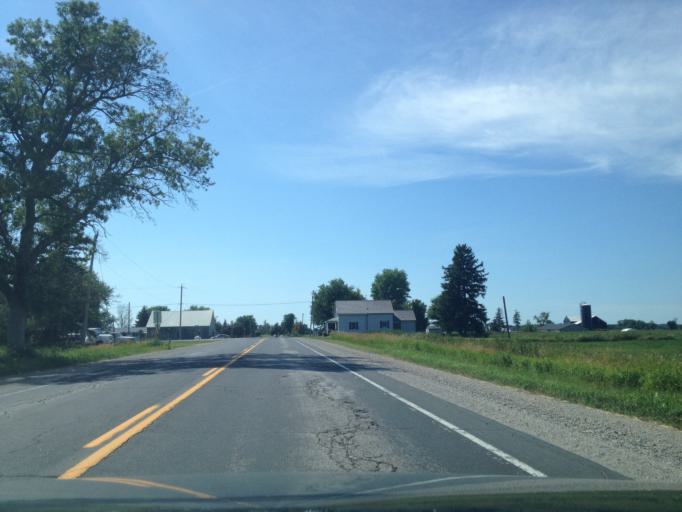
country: CA
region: Ontario
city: Stratford
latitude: 43.5008
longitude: -80.8756
